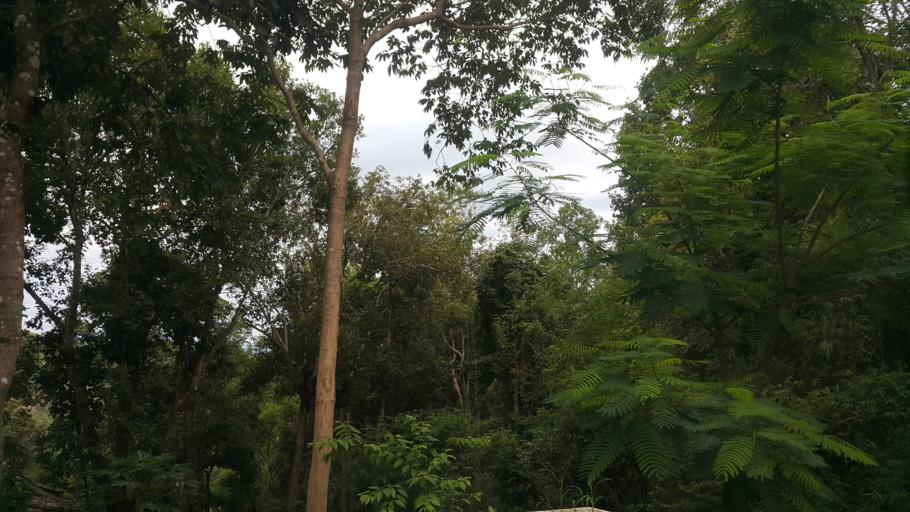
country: TH
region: Loei
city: Na Haeo
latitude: 17.5028
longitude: 101.0892
